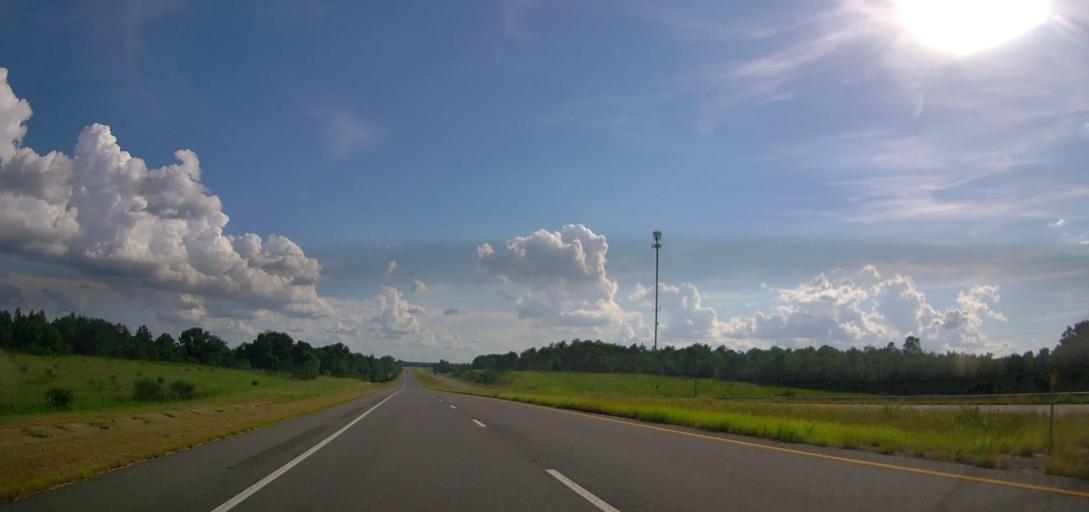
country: US
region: Georgia
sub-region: Talbot County
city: Talbotton
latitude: 32.6058
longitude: -84.4835
